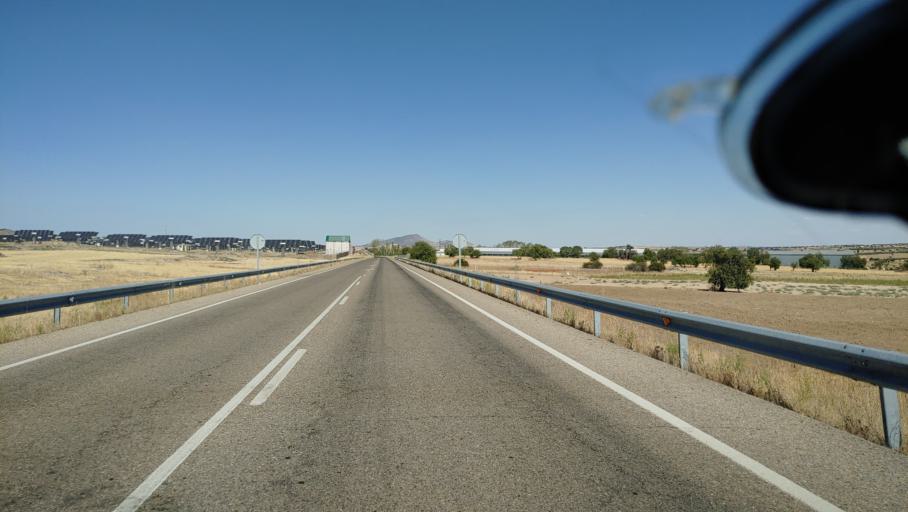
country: ES
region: Castille-La Mancha
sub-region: Province of Toledo
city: Cuerva
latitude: 39.6704
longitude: -4.1967
